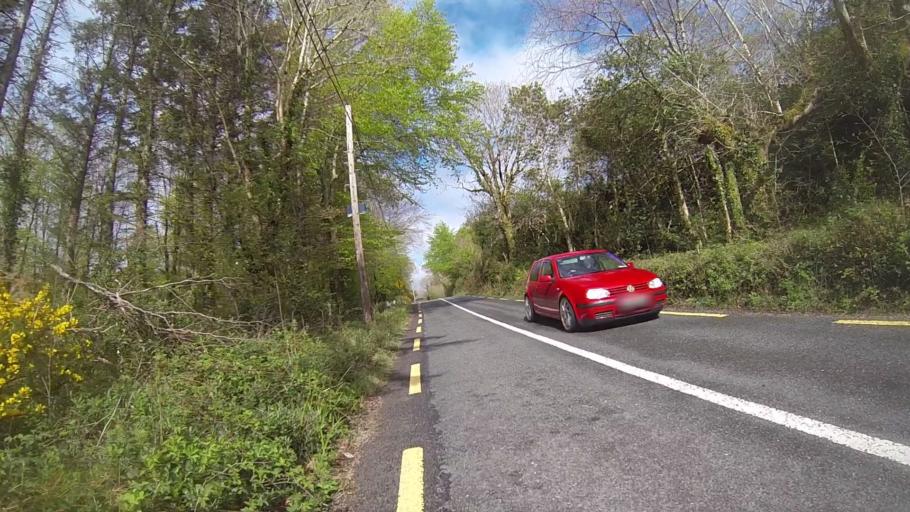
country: IE
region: Munster
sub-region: Ciarrai
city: Kenmare
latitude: 51.8230
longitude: -9.8585
